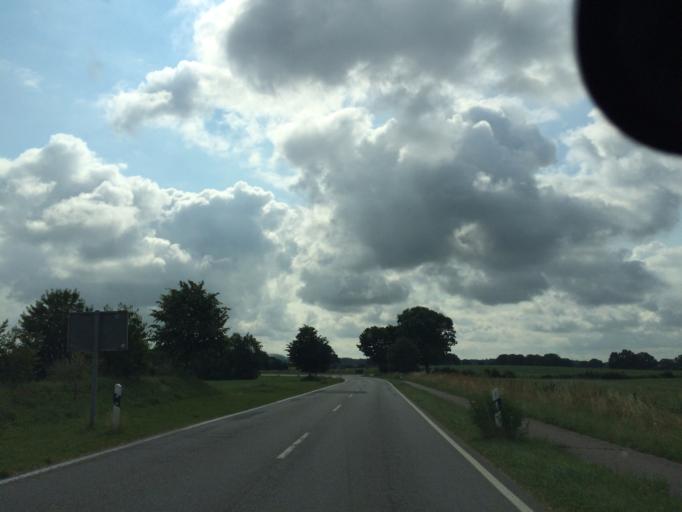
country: DE
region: Schleswig-Holstein
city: Holtsee
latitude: 54.3971
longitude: 9.8570
